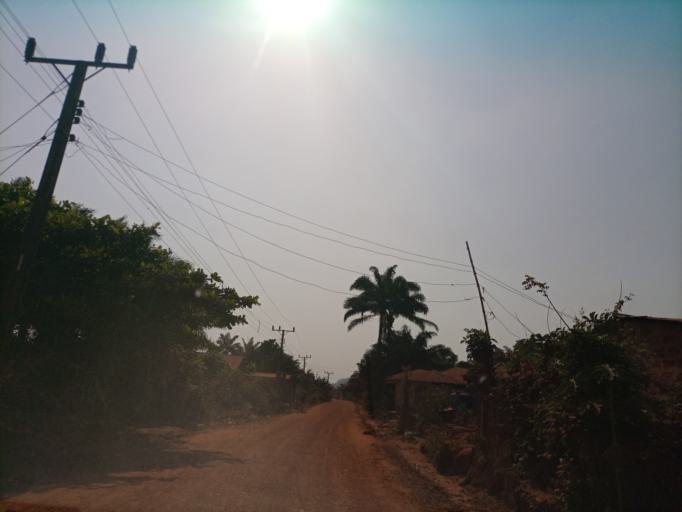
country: NG
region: Enugu
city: Aku
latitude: 6.7086
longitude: 7.3386
